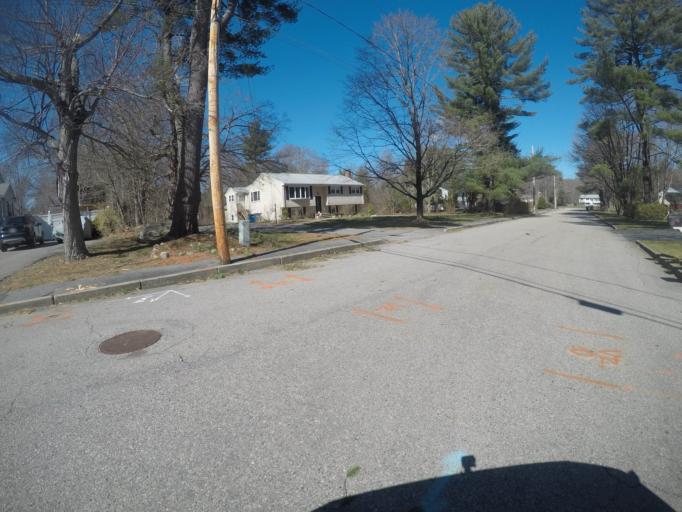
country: US
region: Massachusetts
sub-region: Bristol County
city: Easton
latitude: 42.0082
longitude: -71.1019
